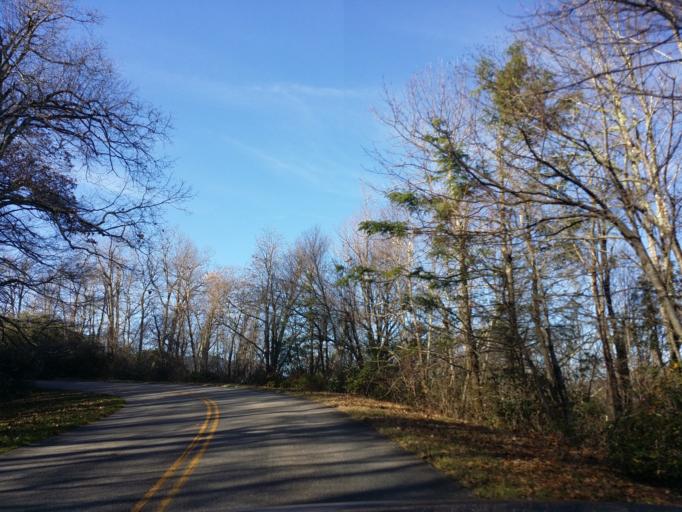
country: US
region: North Carolina
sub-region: Buncombe County
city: Black Mountain
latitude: 35.7384
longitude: -82.1953
